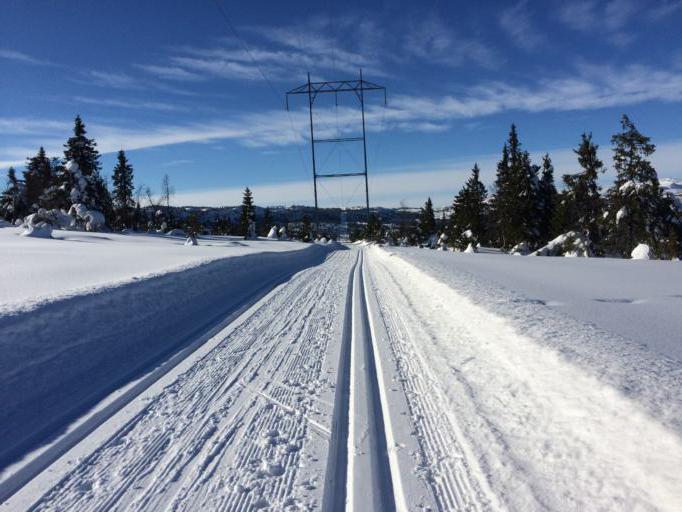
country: NO
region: Oppland
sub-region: Gausdal
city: Segalstad bru
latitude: 61.3158
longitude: 10.1002
